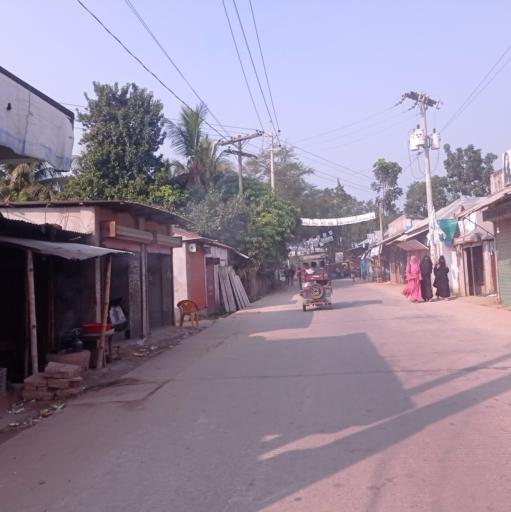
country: BD
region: Dhaka
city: Bhairab Bazar
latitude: 24.0364
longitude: 90.8322
